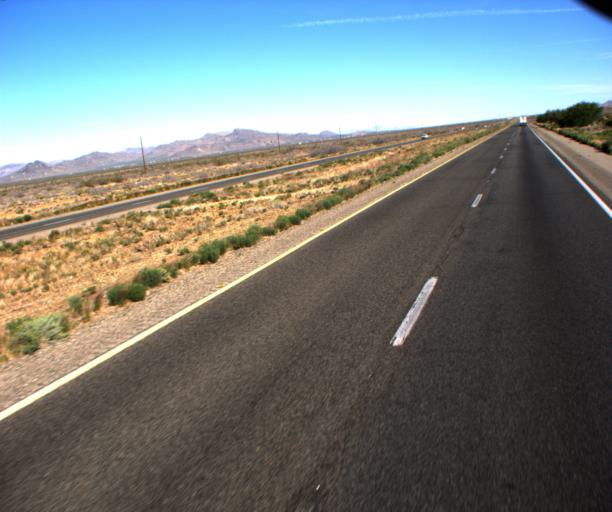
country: US
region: Arizona
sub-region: Mohave County
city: Golden Valley
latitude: 35.2954
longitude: -114.1856
